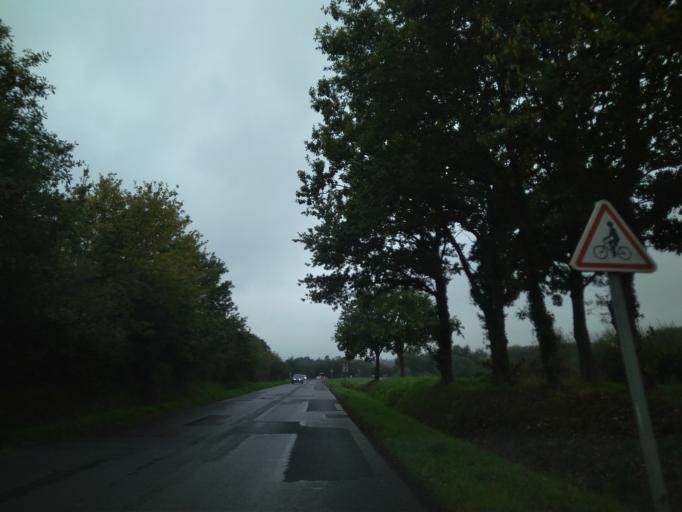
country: FR
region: Brittany
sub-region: Departement d'Ille-et-Vilaine
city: Saint-Gregoire
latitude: 48.1467
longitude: -1.6659
